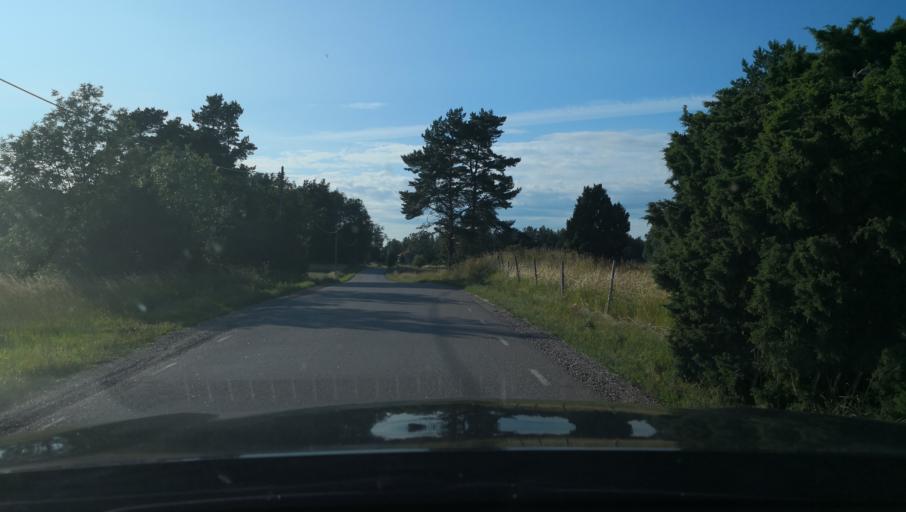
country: SE
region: Uppsala
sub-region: Uppsala Kommun
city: Vattholma
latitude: 59.9292
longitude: 17.8343
